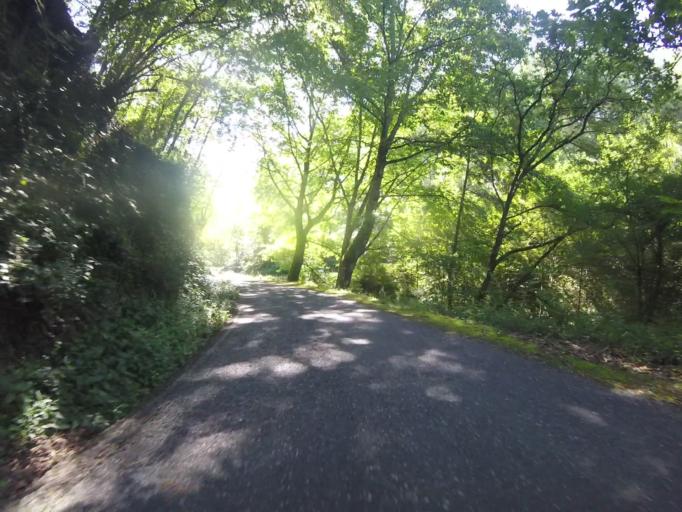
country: ES
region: Navarre
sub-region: Provincia de Navarra
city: Goizueta
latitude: 43.1852
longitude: -1.8238
